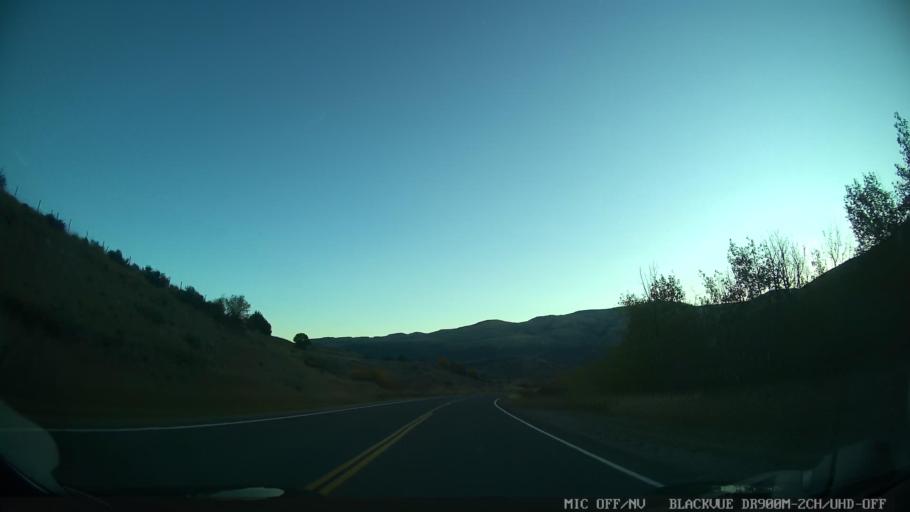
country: US
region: Colorado
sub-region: Eagle County
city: Edwards
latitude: 39.8198
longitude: -106.6496
